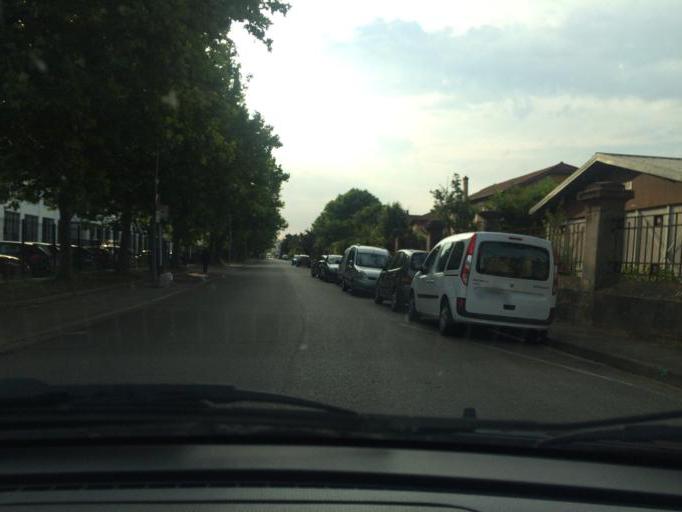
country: FR
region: Rhone-Alpes
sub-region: Departement du Rhone
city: Vaulx-en-Velin
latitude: 45.7590
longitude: 4.9229
